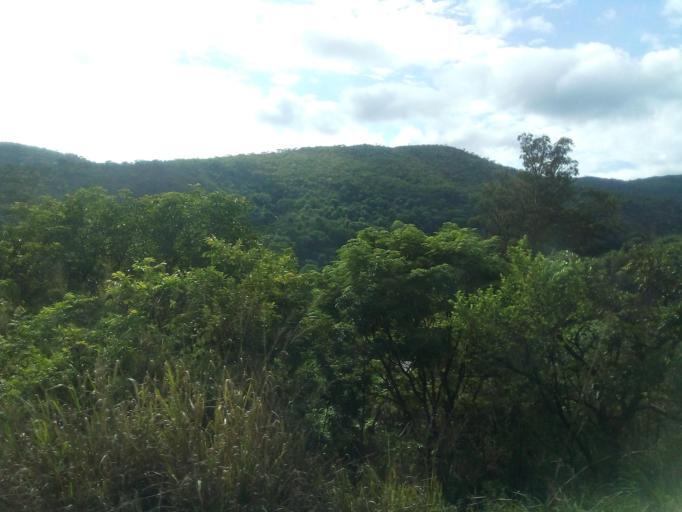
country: BR
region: Minas Gerais
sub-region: Belo Horizonte
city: Belo Horizonte
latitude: -19.8949
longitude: -43.8642
